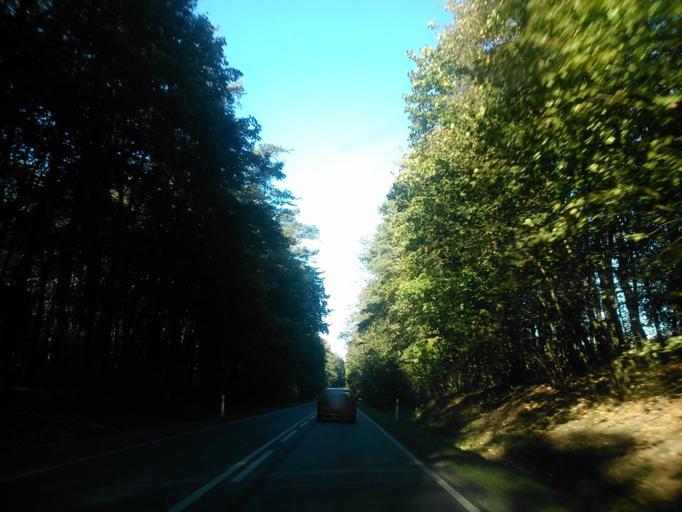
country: PL
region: Kujawsko-Pomorskie
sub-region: Powiat wabrzeski
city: Wabrzezno
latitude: 53.2584
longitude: 19.0107
